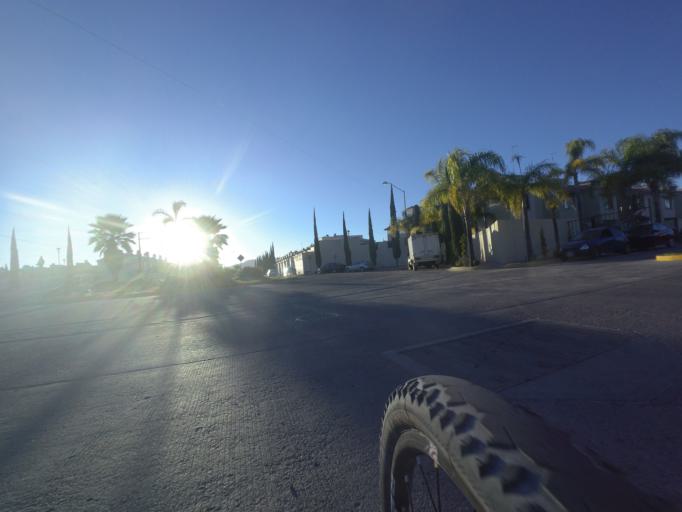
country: MX
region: Aguascalientes
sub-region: Aguascalientes
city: La Loma de los Negritos
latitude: 21.8541
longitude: -102.3437
